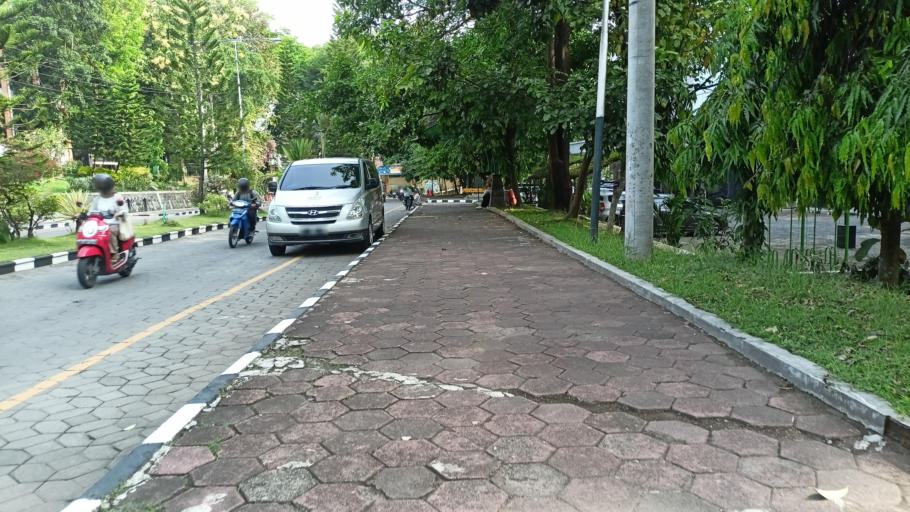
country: ID
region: Central Java
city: Surakarta
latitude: -7.5568
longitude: 110.8568
